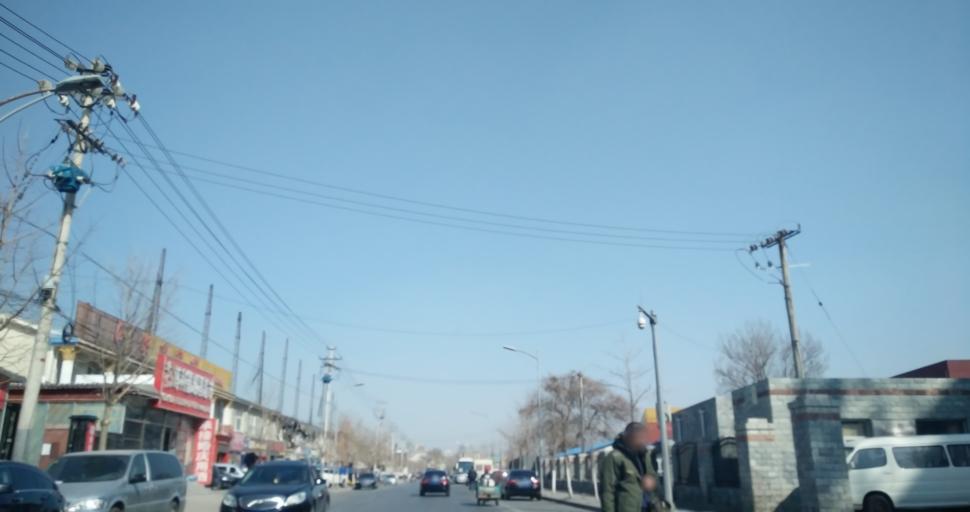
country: CN
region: Beijing
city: Jiugong
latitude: 39.8069
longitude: 116.4383
